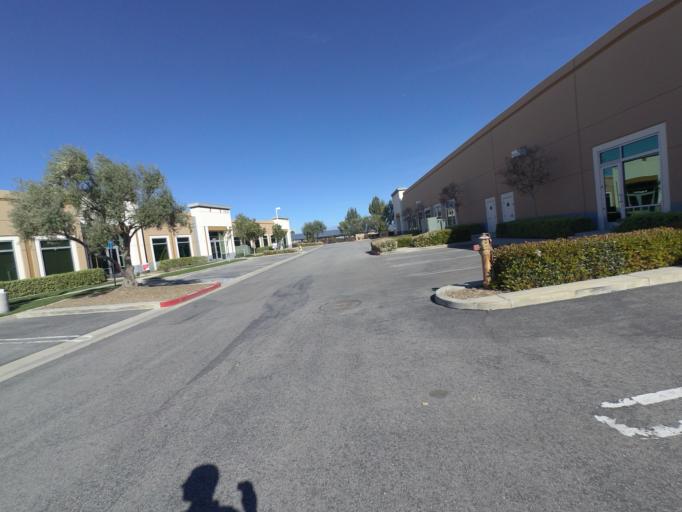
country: US
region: California
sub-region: Riverside County
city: March Air Force Base
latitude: 33.9096
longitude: -117.2855
